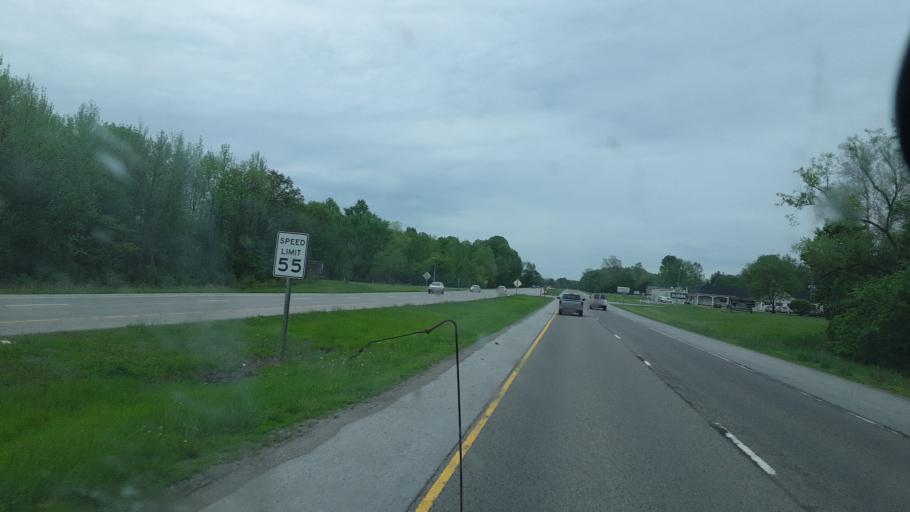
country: US
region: Illinois
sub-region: Jackson County
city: Murphysboro
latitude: 37.7653
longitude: -89.3142
